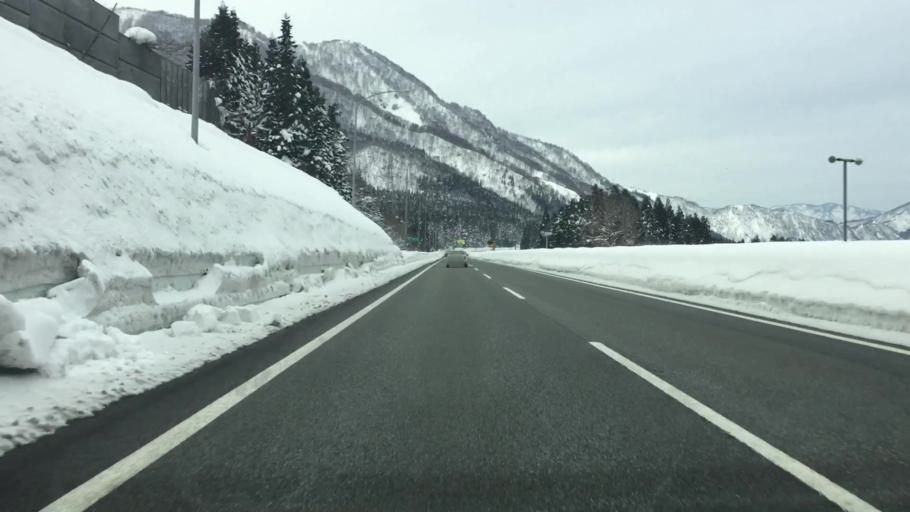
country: JP
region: Niigata
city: Shiozawa
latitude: 36.8775
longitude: 138.8591
